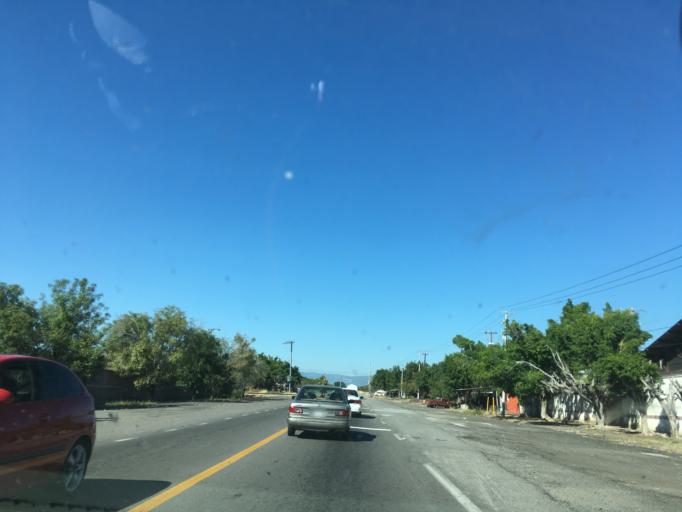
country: MX
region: Michoacan
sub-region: Gabriel Zamora
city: Lombardia
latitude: 19.0955
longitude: -102.0579
